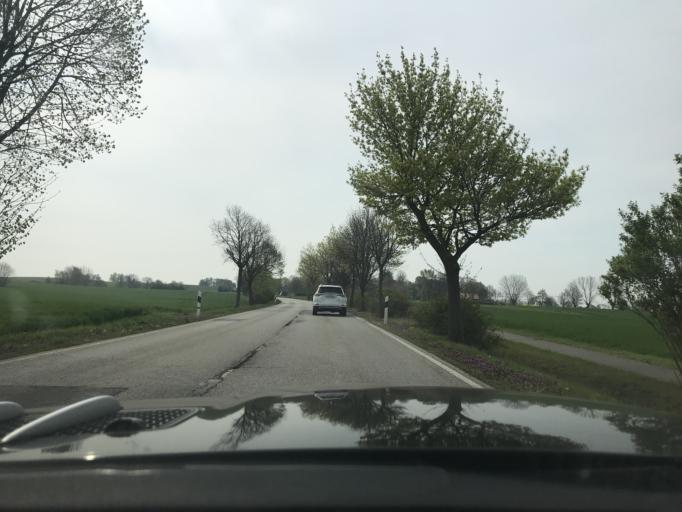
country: DE
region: Schleswig-Holstein
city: Heringsdorf
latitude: 54.2935
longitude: 11.0145
